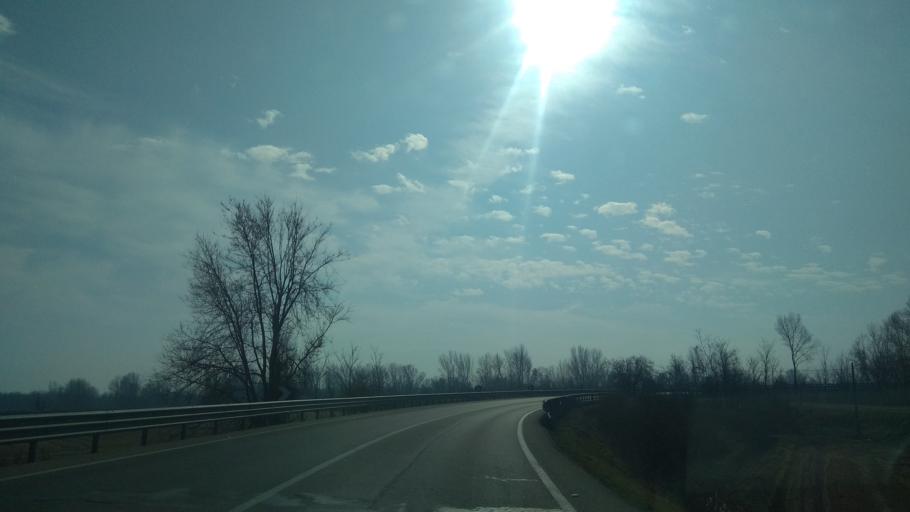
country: IT
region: Piedmont
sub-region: Provincia di Vercelli
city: Collobiano
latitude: 45.3915
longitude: 8.3551
